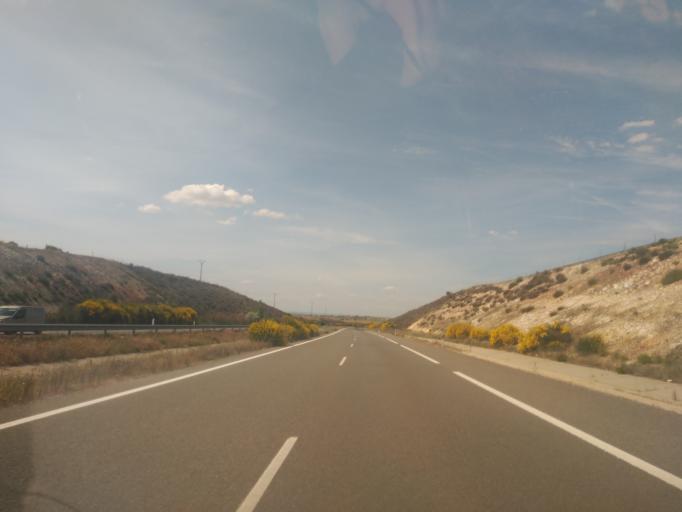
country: ES
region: Castille and Leon
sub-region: Provincia de Salamanca
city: Mozarbez
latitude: 40.8415
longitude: -5.6385
